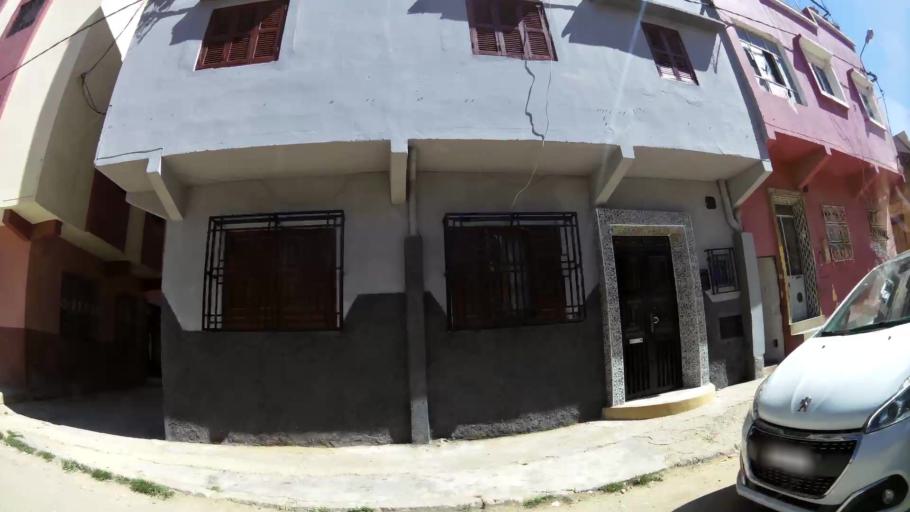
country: MA
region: Meknes-Tafilalet
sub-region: Meknes
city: Meknes
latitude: 33.9111
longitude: -5.5346
